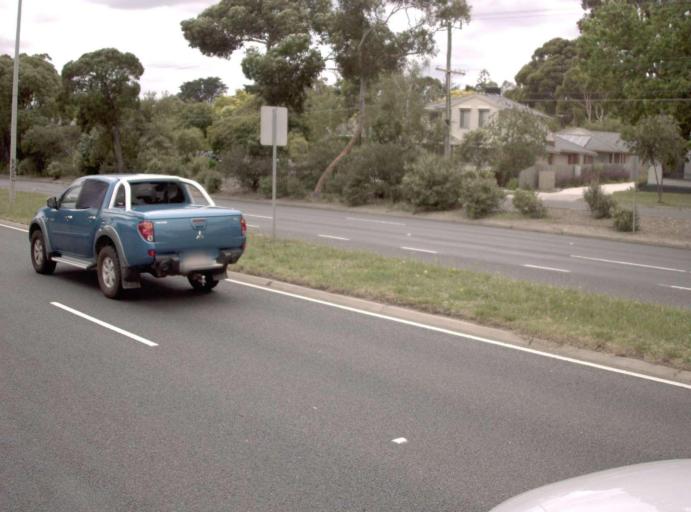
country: AU
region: Victoria
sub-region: Maroondah
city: Croydon Hills
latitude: -37.7888
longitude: 145.2693
